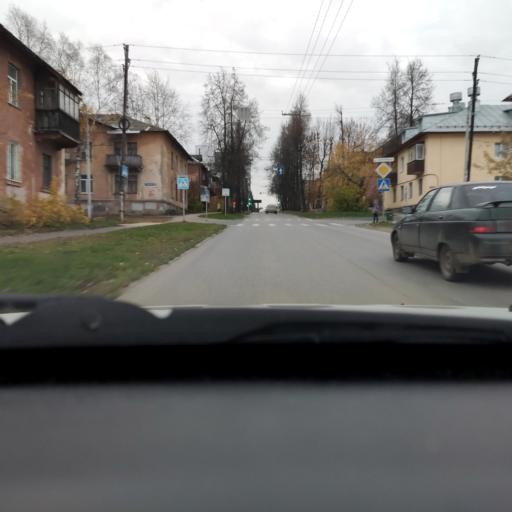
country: RU
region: Perm
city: Kondratovo
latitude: 57.9731
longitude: 56.1749
